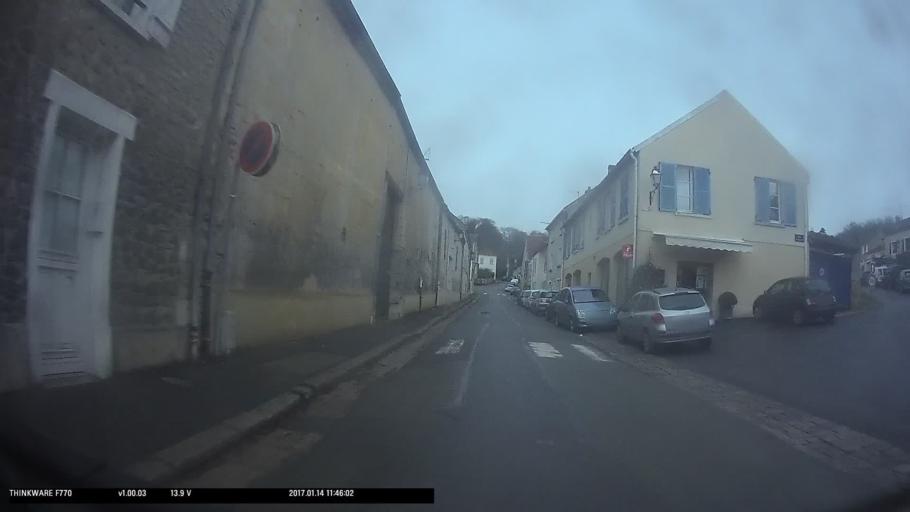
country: FR
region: Ile-de-France
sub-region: Departement du Val-d'Oise
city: Vigny
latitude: 49.0784
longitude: 1.9281
